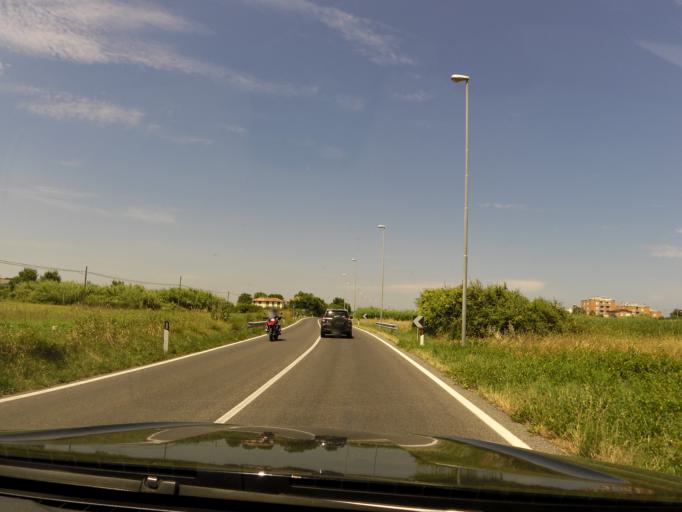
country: IT
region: The Marches
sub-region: Provincia di Pesaro e Urbino
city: Marotta
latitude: 43.7936
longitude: 13.1003
